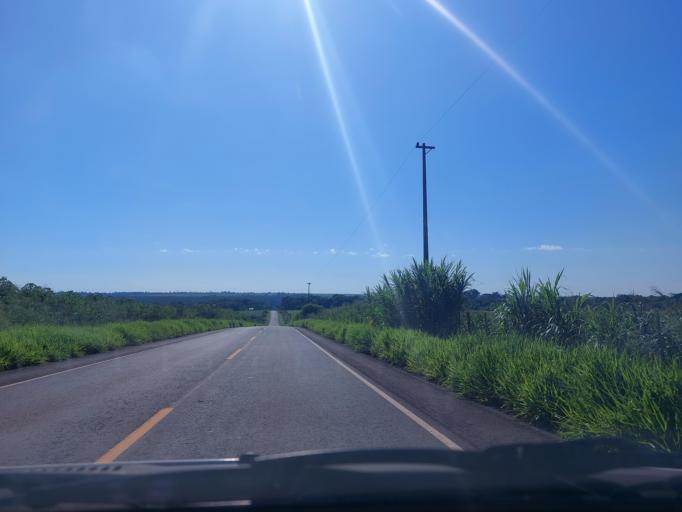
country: PY
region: San Pedro
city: Guayaybi
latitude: -24.3066
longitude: -56.1494
